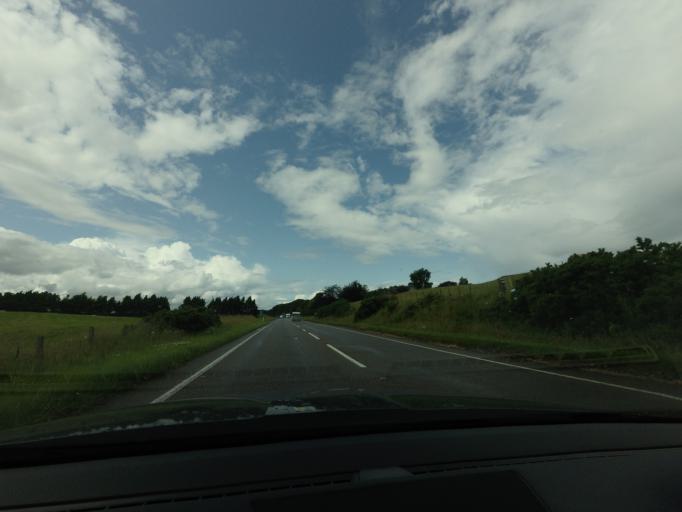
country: GB
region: Scotland
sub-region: Moray
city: Lhanbryd
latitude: 57.6291
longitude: -3.1708
